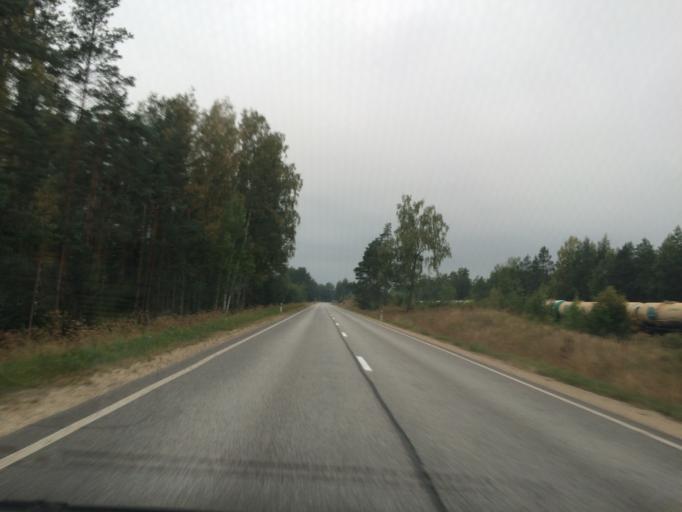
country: LV
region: Varaklani
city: Varaklani
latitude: 56.5269
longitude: 26.5202
